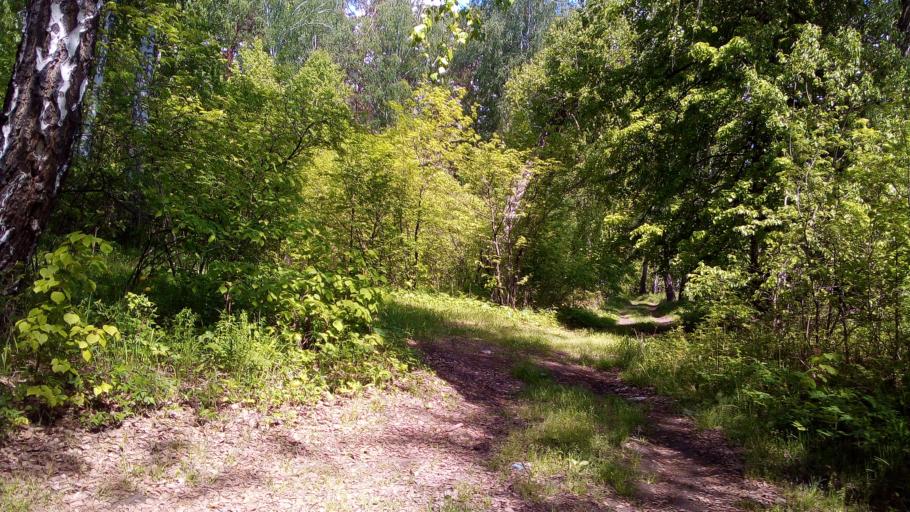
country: RU
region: Chelyabinsk
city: Chebarkul'
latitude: 55.0827
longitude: 60.3820
